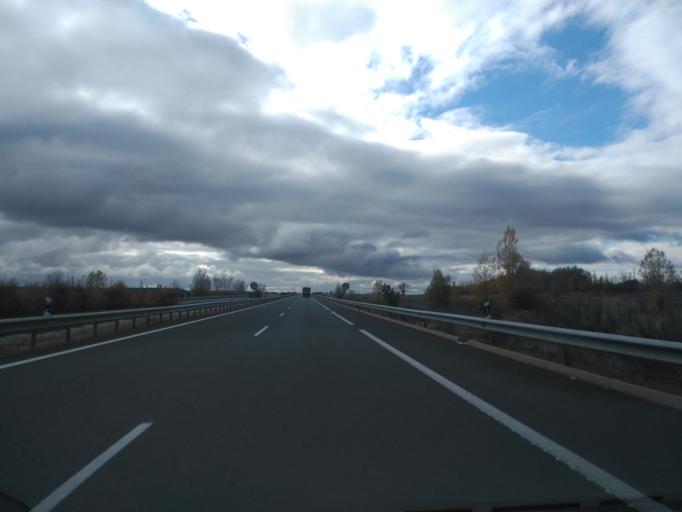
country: ES
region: Castille and Leon
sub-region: Provincia de Palencia
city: Pina de Campos
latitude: 42.2343
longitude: -4.4277
